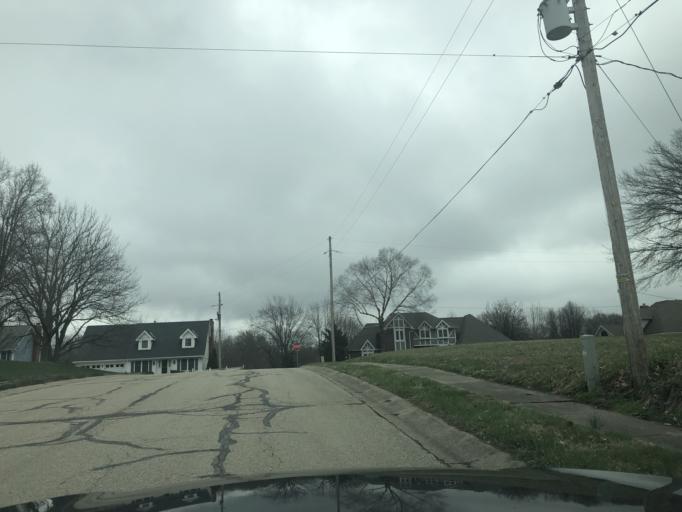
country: US
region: Kansas
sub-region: Leavenworth County
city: Leavenworth
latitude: 39.2832
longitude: -94.9145
